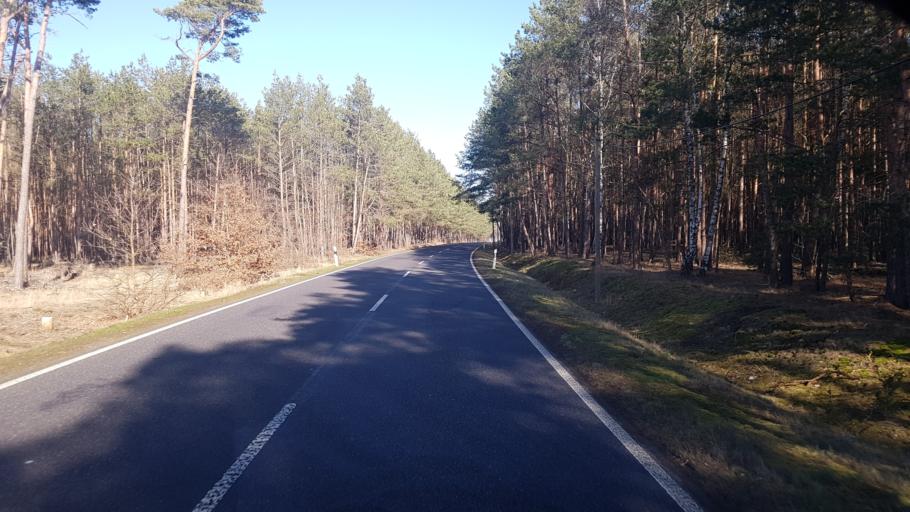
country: DE
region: Brandenburg
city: Ihlow
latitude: 51.8079
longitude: 13.3232
